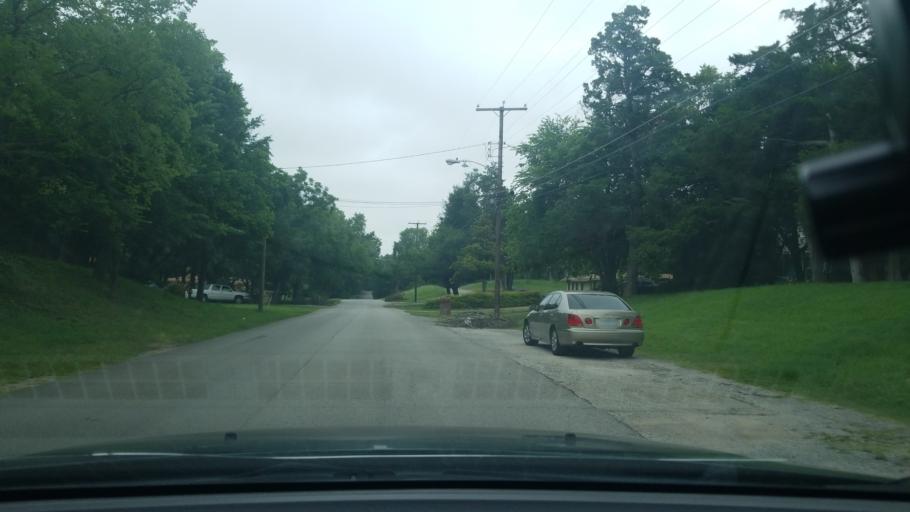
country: US
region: Texas
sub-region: Dallas County
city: Balch Springs
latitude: 32.7644
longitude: -96.6909
